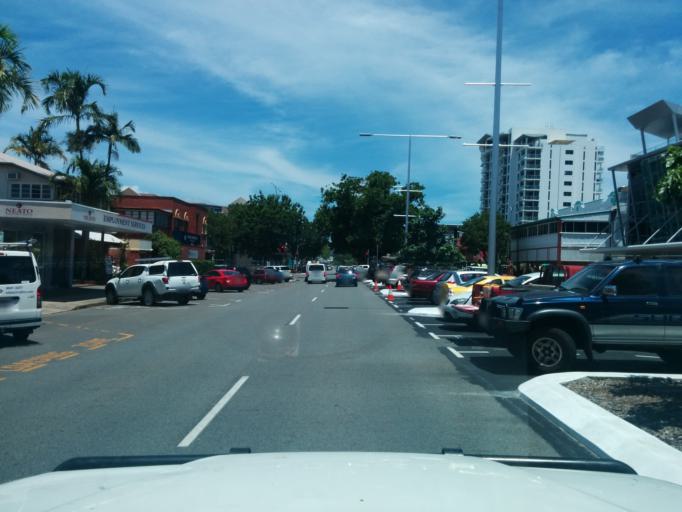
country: AU
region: Queensland
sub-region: Cairns
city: Cairns
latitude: -16.9205
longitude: 145.7728
